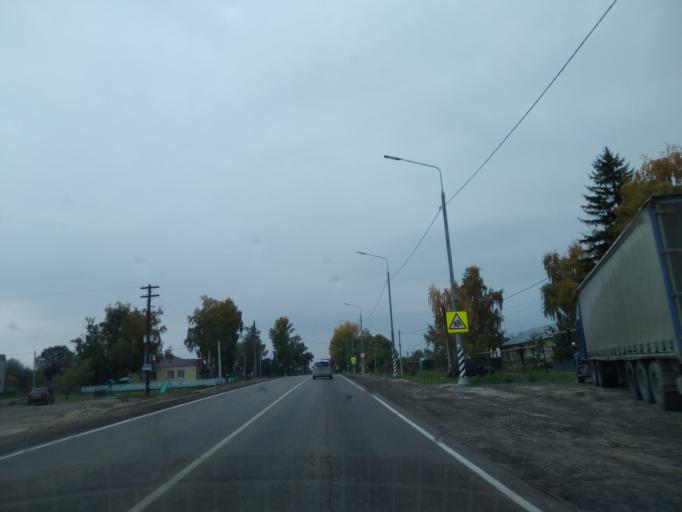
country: RU
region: Lipetsk
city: Zadonsk
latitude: 52.4137
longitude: 38.8696
